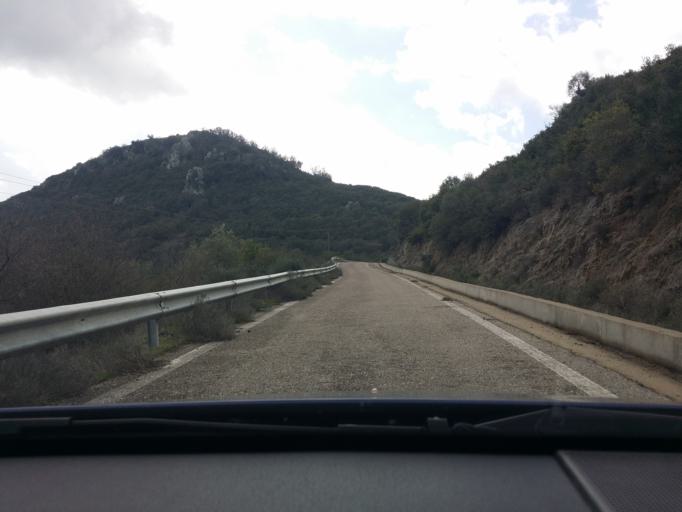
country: GR
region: West Greece
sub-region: Nomos Aitolias kai Akarnanias
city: Fitiai
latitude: 38.6554
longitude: 21.1975
